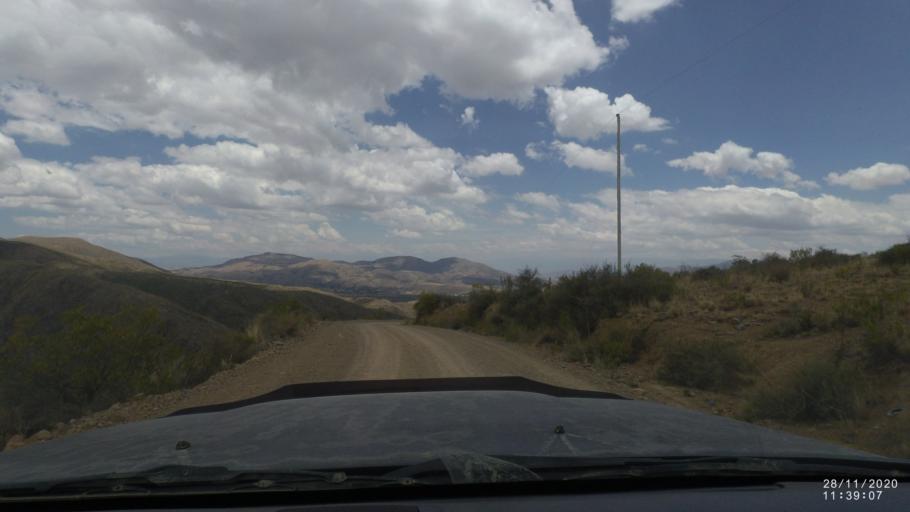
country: BO
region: Cochabamba
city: Tarata
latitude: -17.6767
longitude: -66.0444
